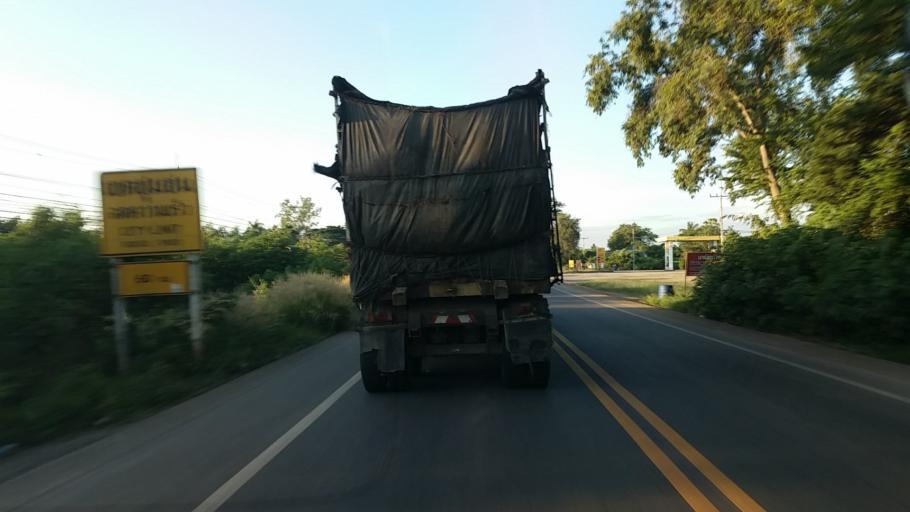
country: TH
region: Lop Buri
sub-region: Amphoe Lam Sonthi
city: Lam Sonthi
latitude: 15.2654
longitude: 101.3361
